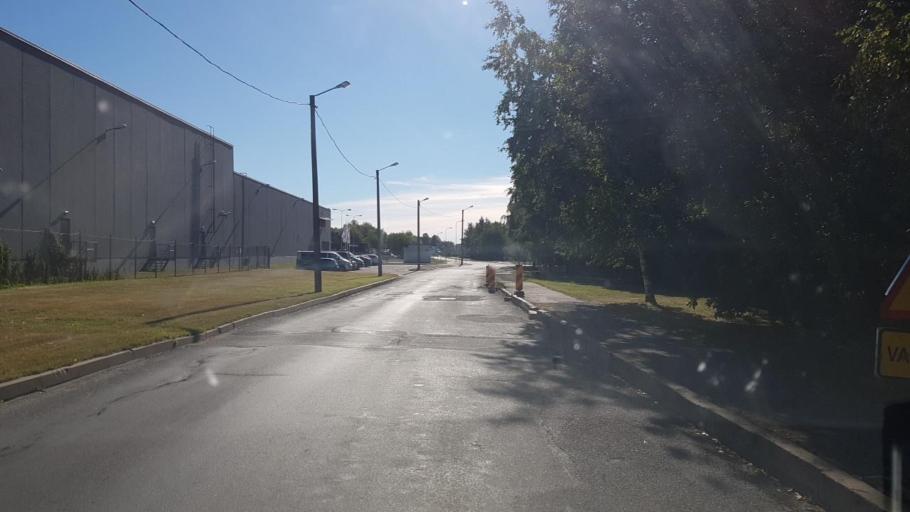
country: EE
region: Harju
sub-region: Tallinna linn
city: Tallinn
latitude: 59.4078
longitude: 24.8146
